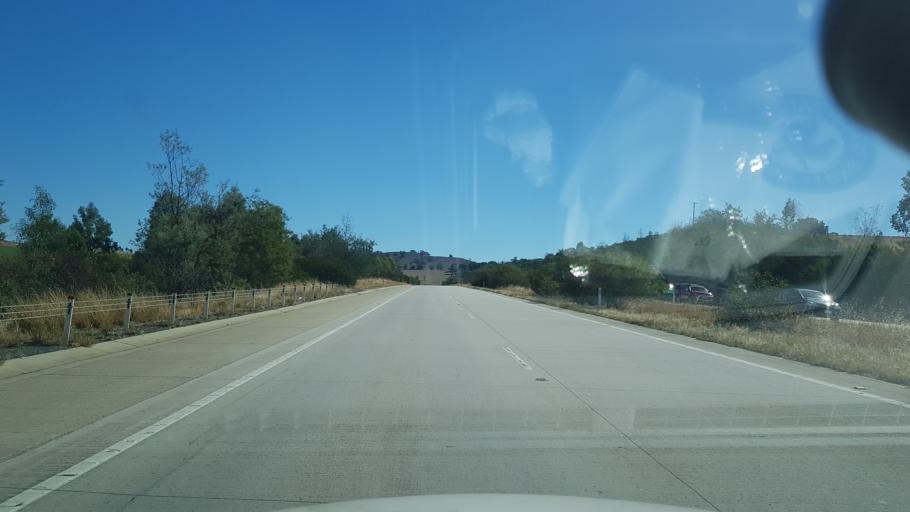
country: AU
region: New South Wales
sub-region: Albury Municipality
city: Lavington
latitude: -35.9155
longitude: 147.1121
